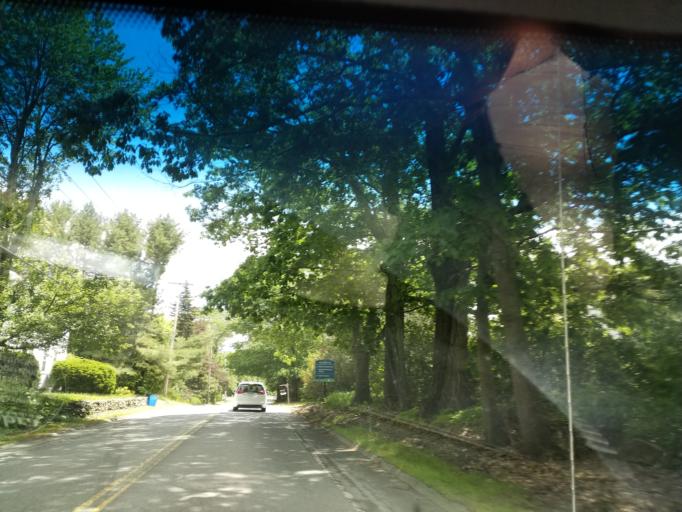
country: US
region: Maine
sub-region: Cumberland County
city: Falmouth
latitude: 43.7328
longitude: -70.2792
